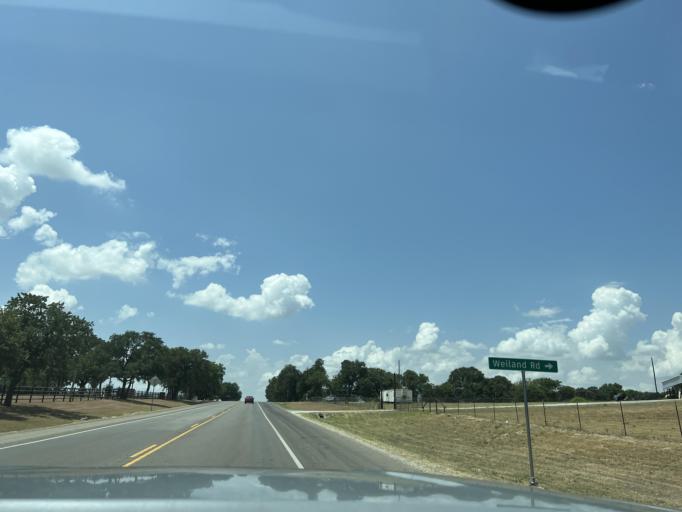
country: US
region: Texas
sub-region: Parker County
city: Springtown
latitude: 32.8689
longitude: -97.7454
